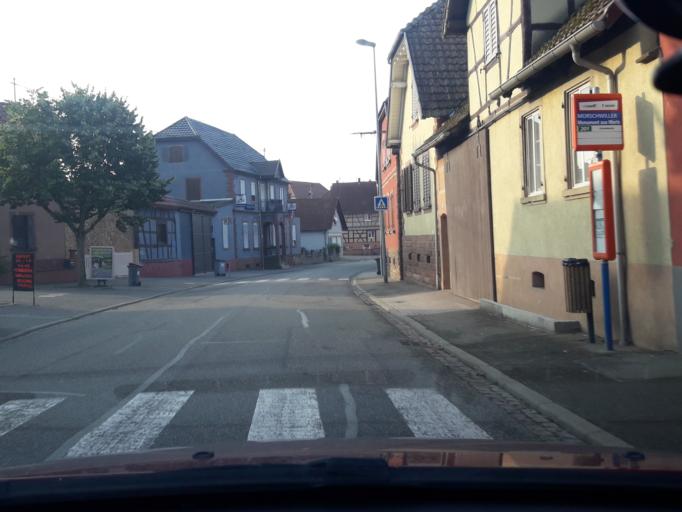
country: FR
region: Alsace
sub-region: Departement du Bas-Rhin
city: Pfaffenhoffen
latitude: 48.8200
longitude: 7.6264
